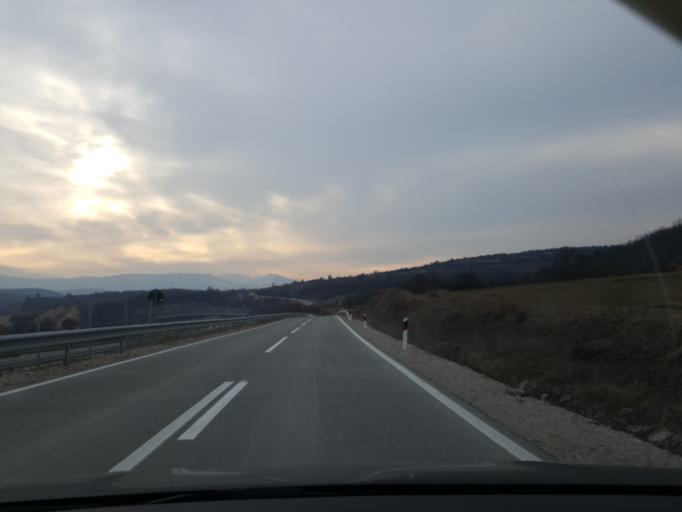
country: RS
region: Central Serbia
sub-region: Pirotski Okrug
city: Bela Palanka
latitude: 43.2316
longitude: 22.4428
